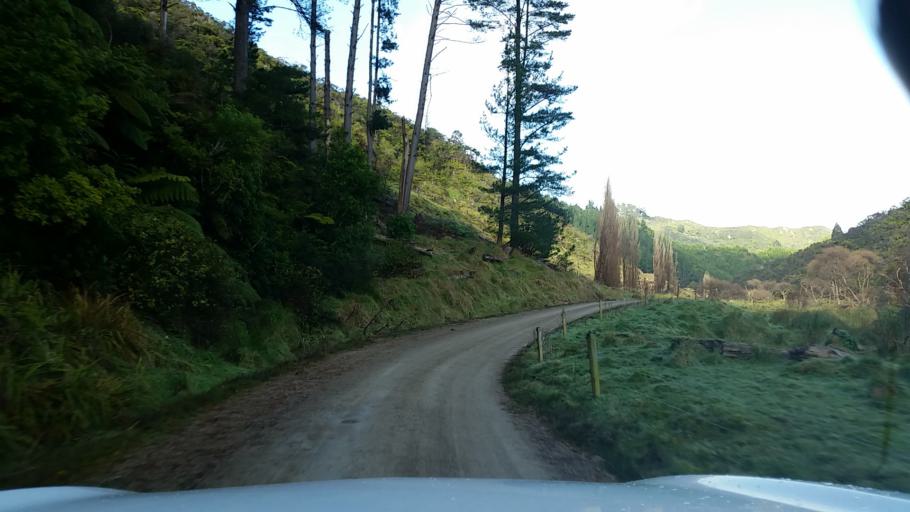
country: NZ
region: Taranaki
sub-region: South Taranaki District
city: Patea
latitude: -39.6847
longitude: 174.7639
